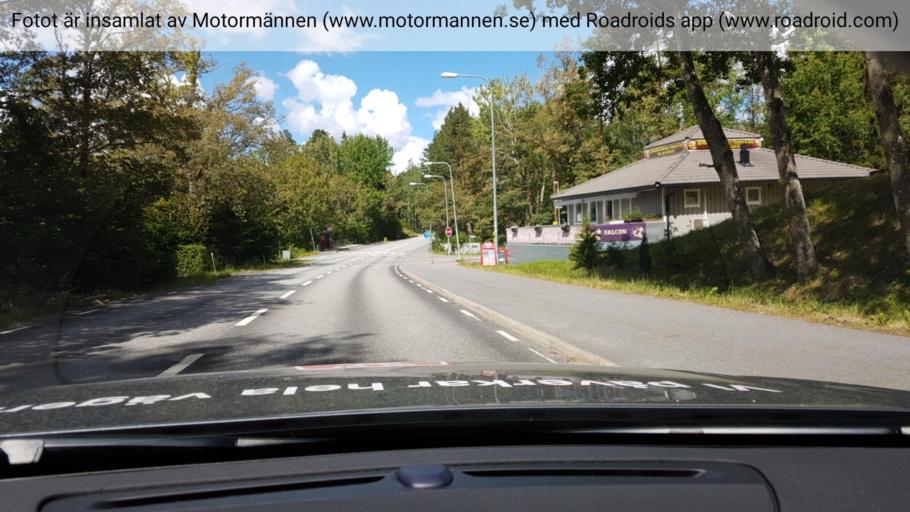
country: SE
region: Stockholm
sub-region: Varmdo Kommun
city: Hemmesta
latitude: 59.3348
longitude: 18.4896
